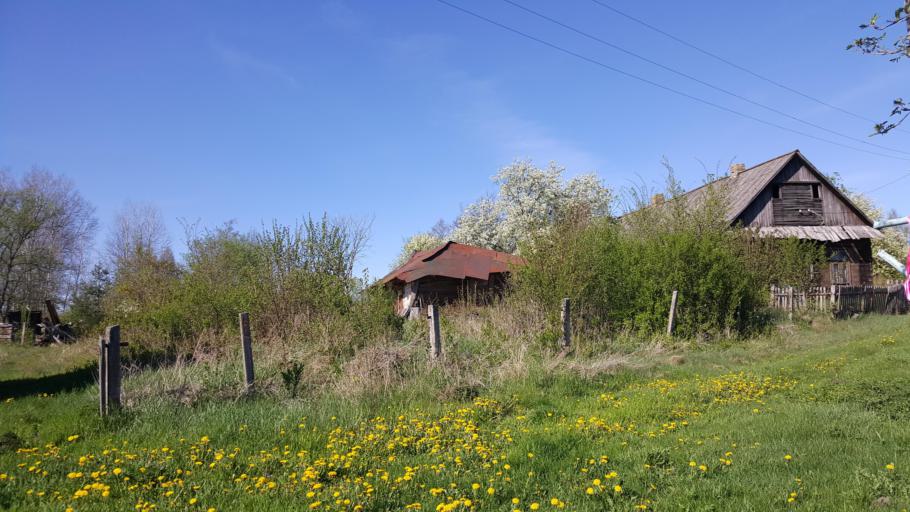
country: BY
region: Brest
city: Kamyanyets
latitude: 52.4350
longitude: 23.8728
